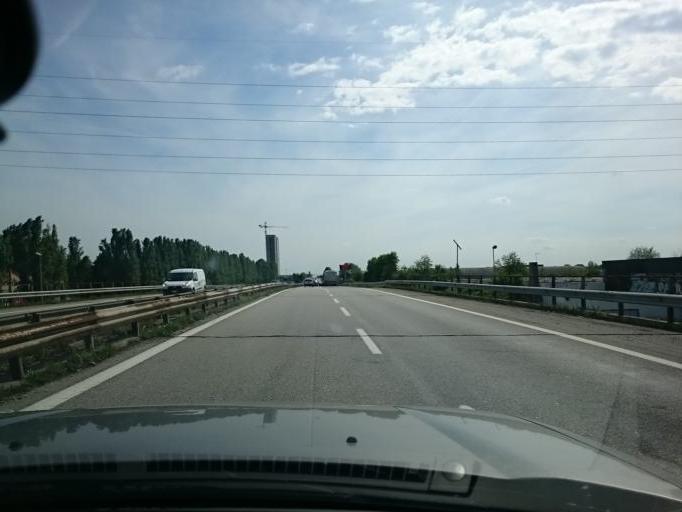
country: IT
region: Veneto
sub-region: Provincia di Padova
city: Noventa
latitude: 45.3961
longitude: 11.9286
